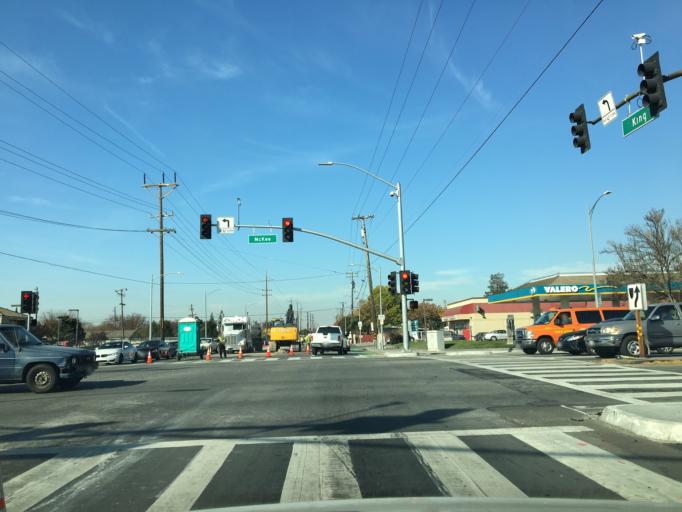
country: US
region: California
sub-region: Santa Clara County
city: Alum Rock
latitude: 37.3580
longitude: -121.8606
